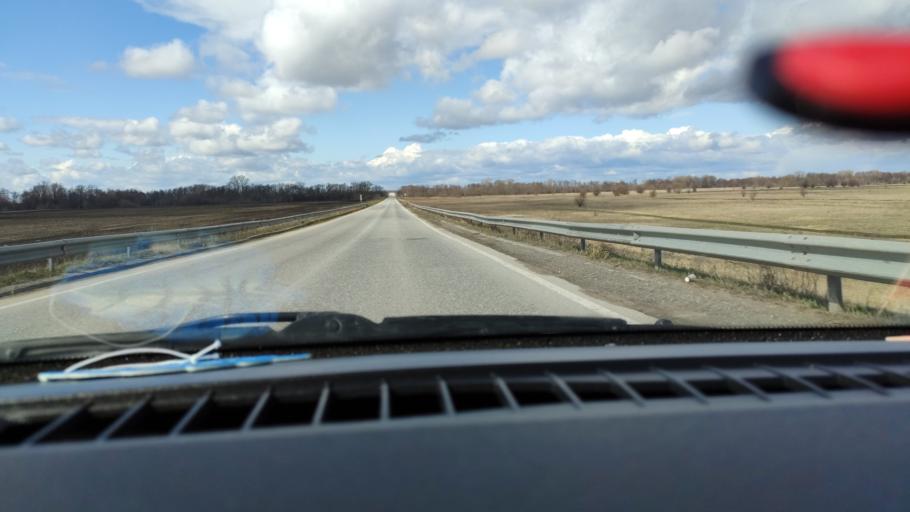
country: RU
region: Samara
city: Tol'yatti
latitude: 53.7823
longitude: 49.5030
